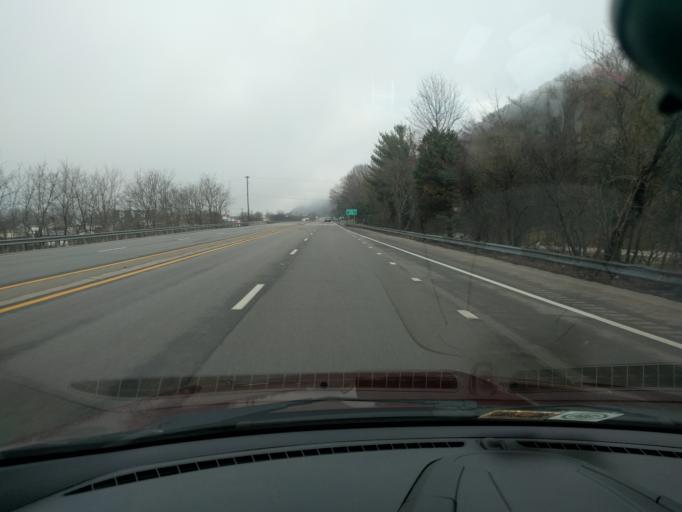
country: US
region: West Virginia
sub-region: Kanawha County
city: Belle
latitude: 38.2286
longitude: -81.5328
